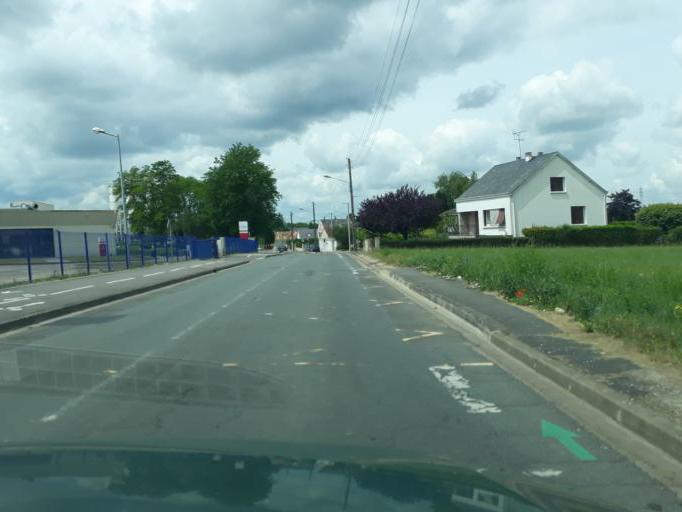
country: FR
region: Centre
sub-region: Departement du Loiret
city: La Chapelle-Saint-Mesmin
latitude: 47.8978
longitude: 1.8320
